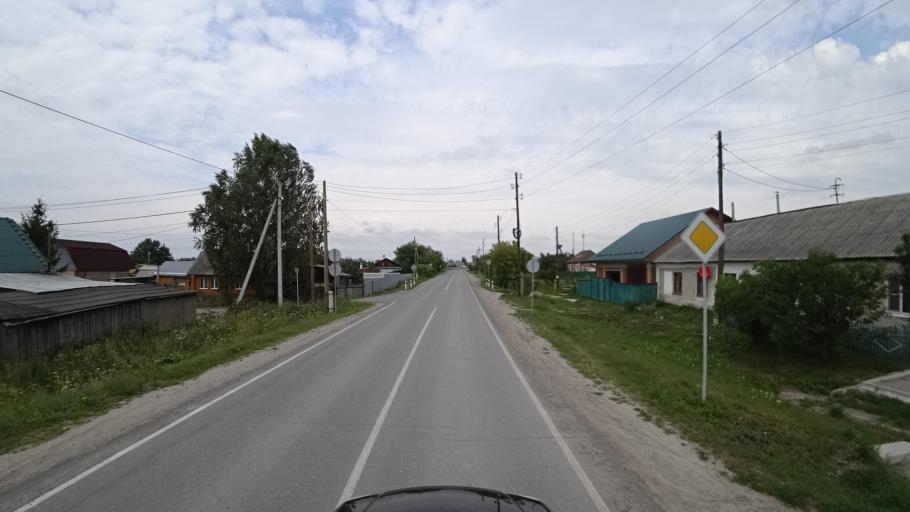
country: RU
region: Sverdlovsk
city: Kamyshlov
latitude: 56.8513
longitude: 62.7413
